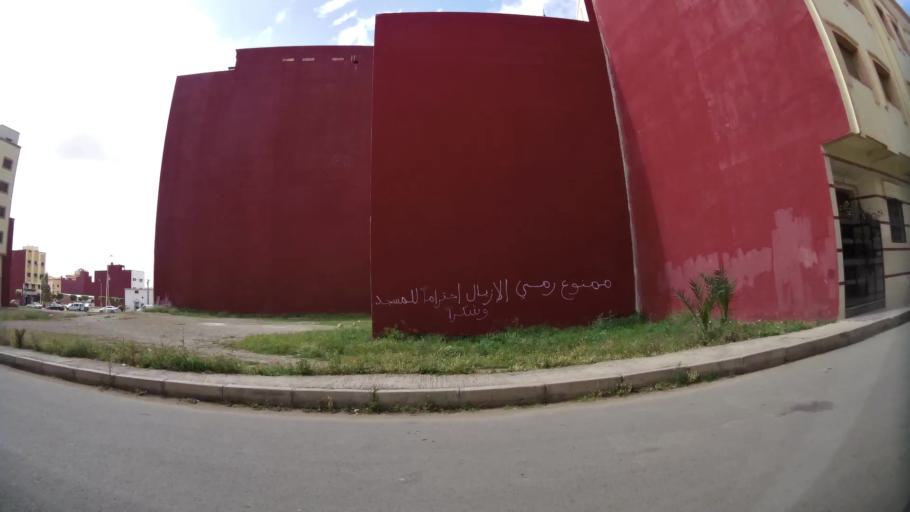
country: MA
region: Oriental
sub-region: Nador
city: Nador
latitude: 35.1617
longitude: -2.9295
